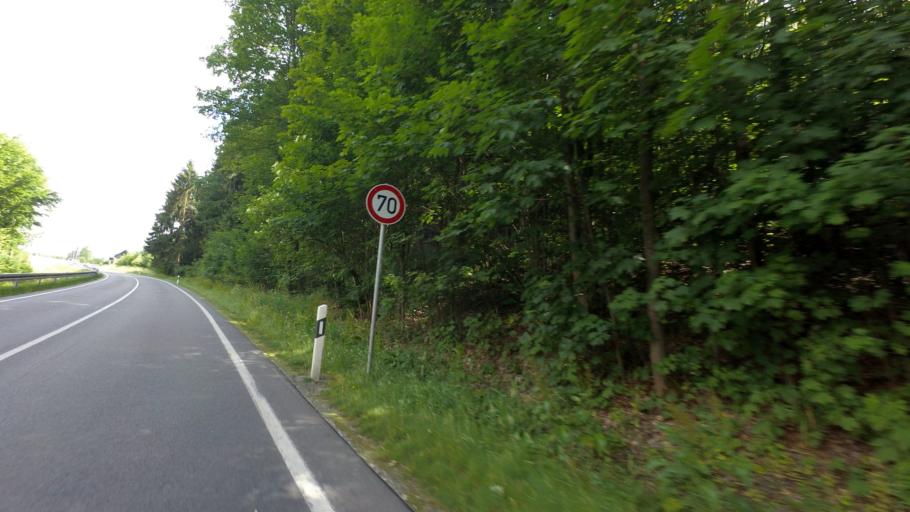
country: DE
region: Saxony
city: Rammenau
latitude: 51.1694
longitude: 14.1417
